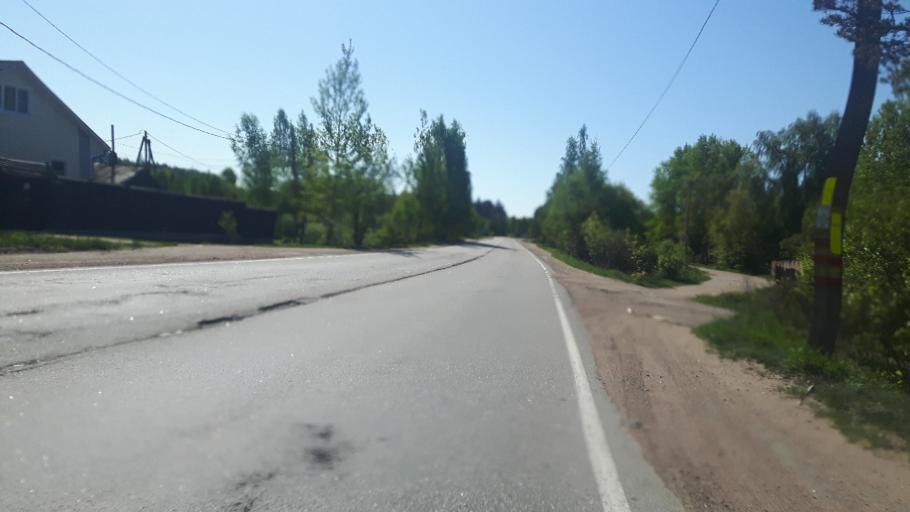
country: RU
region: Leningrad
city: Vyborg
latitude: 60.6517
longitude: 28.7451
